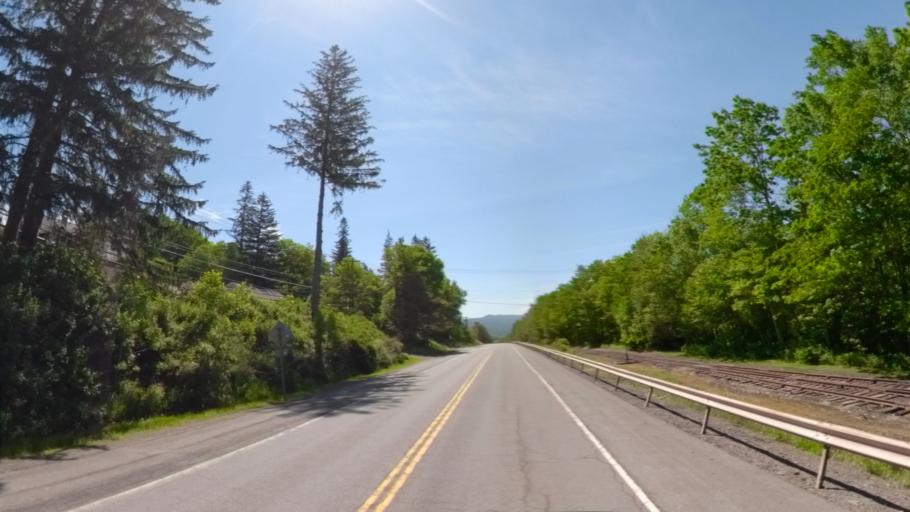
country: US
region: New York
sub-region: Delaware County
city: Stamford
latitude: 42.1462
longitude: -74.4930
